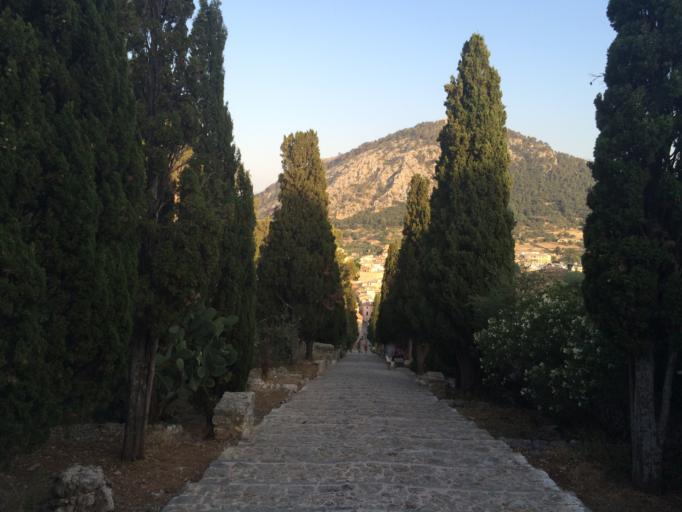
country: ES
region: Balearic Islands
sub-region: Illes Balears
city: Pollenca
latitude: 39.8799
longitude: 3.0126
